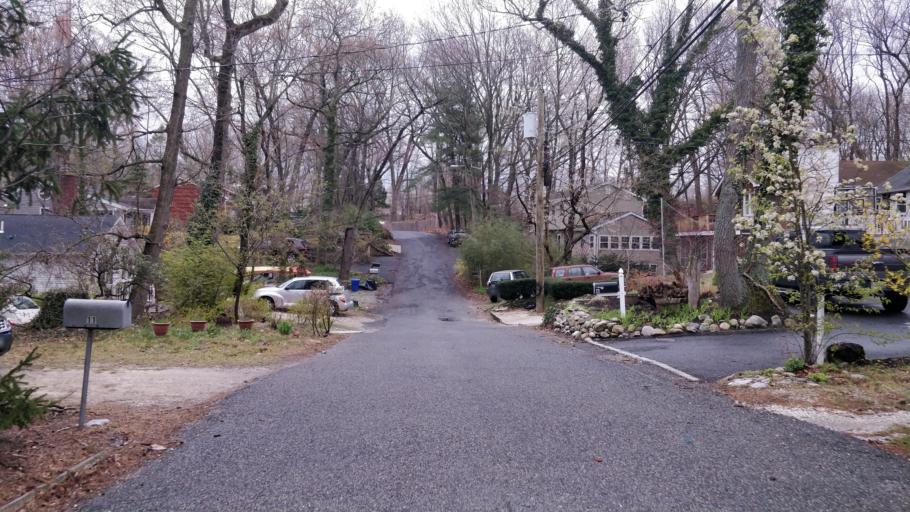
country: US
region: New York
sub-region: Suffolk County
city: Port Jefferson
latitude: 40.9505
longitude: -73.0829
